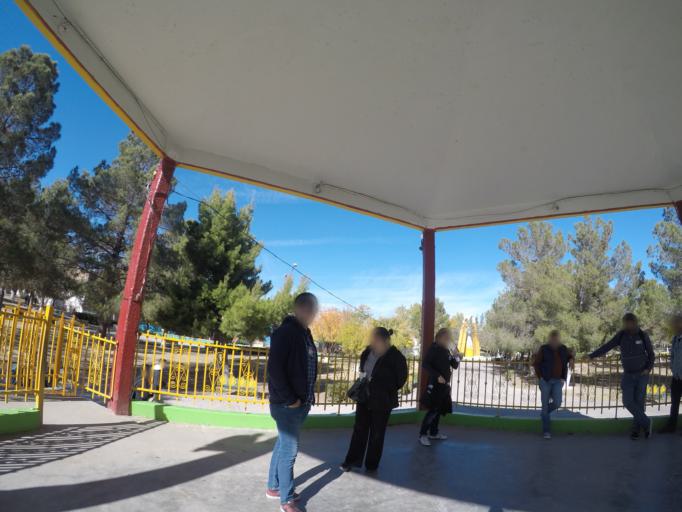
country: MX
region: Chihuahua
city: Ciudad Juarez
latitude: 31.7361
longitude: -106.4611
